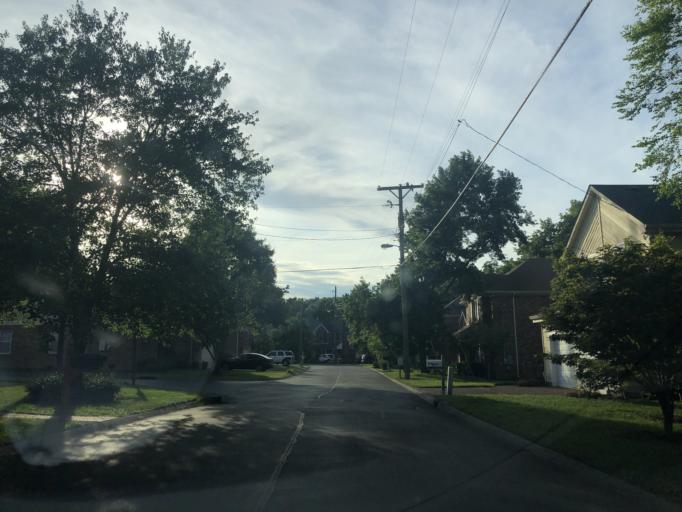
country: US
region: Tennessee
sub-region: Davidson County
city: Belle Meade
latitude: 36.0674
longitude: -86.9385
